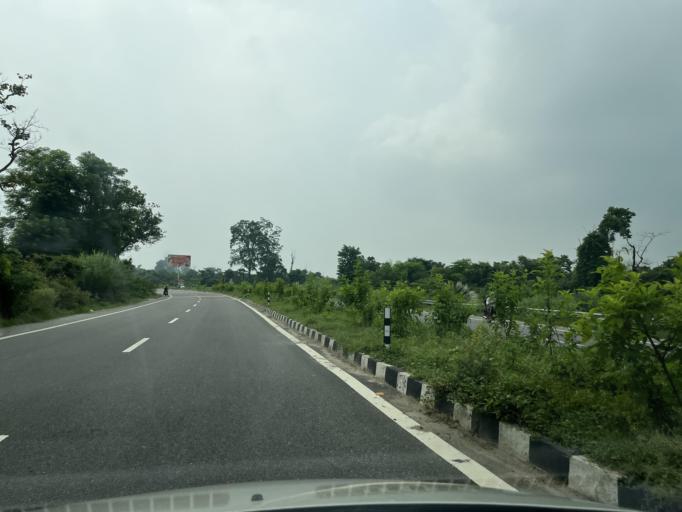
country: IN
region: Uttarakhand
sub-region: Dehradun
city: Raiwala
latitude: 30.0589
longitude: 78.2139
